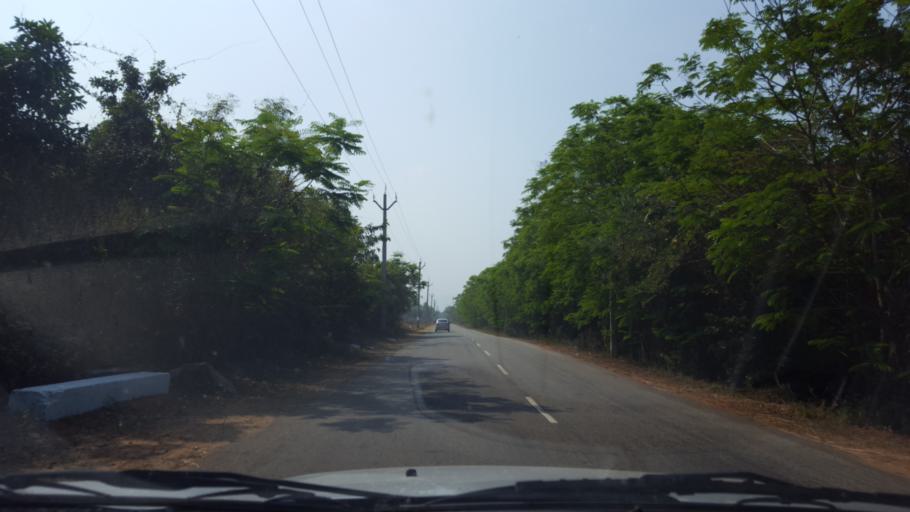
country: IN
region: Andhra Pradesh
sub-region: Vishakhapatnam
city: Vepagunta
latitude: 17.8447
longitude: 83.2666
